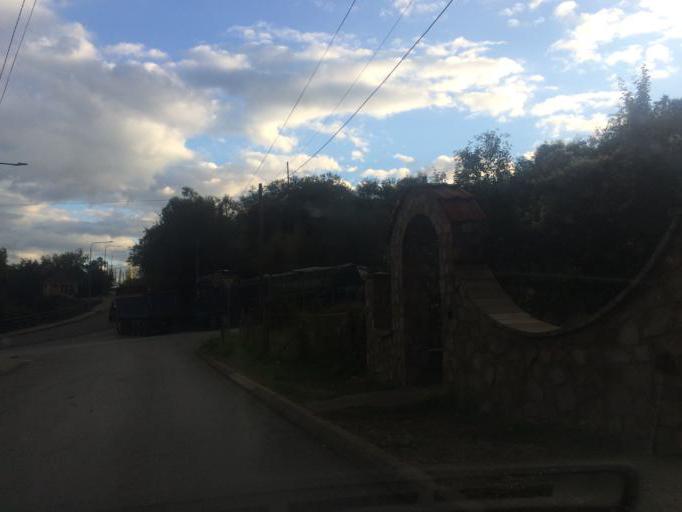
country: MK
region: Makedonska Kamenica
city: Makedonska Kamenica
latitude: 42.0236
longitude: 22.5859
